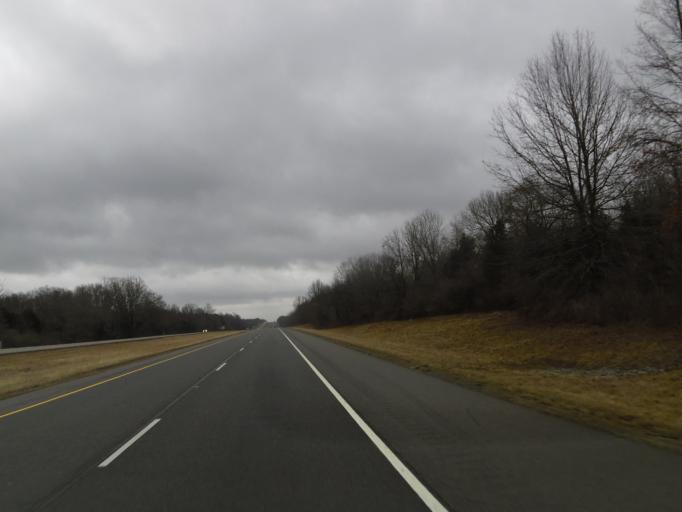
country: US
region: Illinois
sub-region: Johnson County
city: Vienna
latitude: 37.3995
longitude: -88.8513
